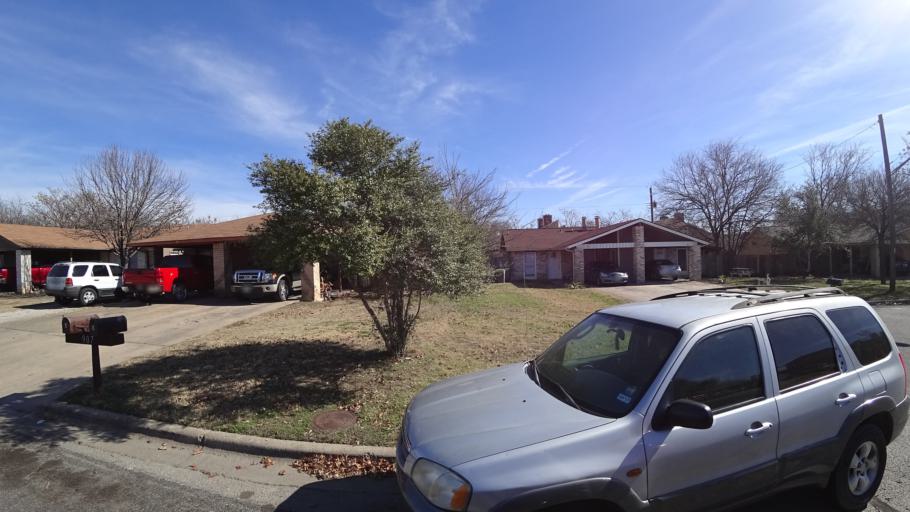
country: US
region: Texas
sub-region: Travis County
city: Wells Branch
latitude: 30.3702
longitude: -97.6965
